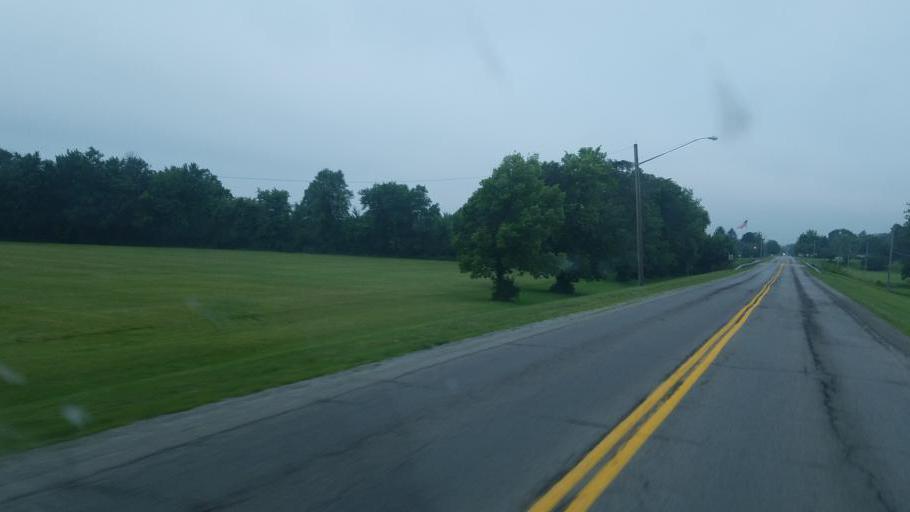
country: US
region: Ohio
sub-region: Fayette County
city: Washington Court House
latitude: 39.5407
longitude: -83.4125
